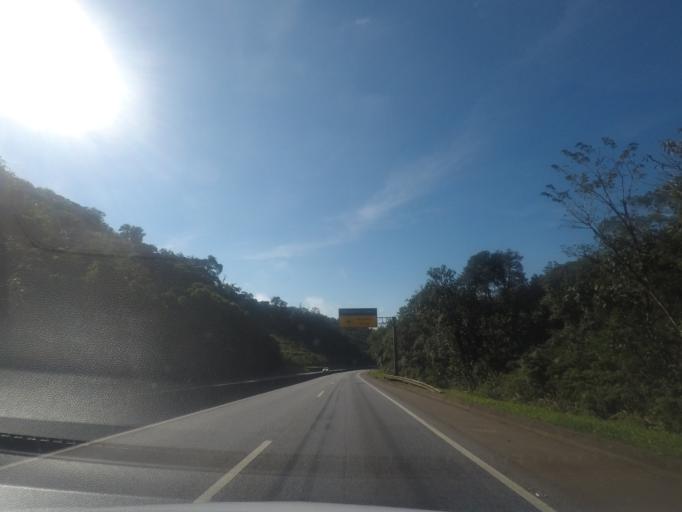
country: BR
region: Parana
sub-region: Piraquara
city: Piraquara
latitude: -25.5918
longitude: -48.9172
